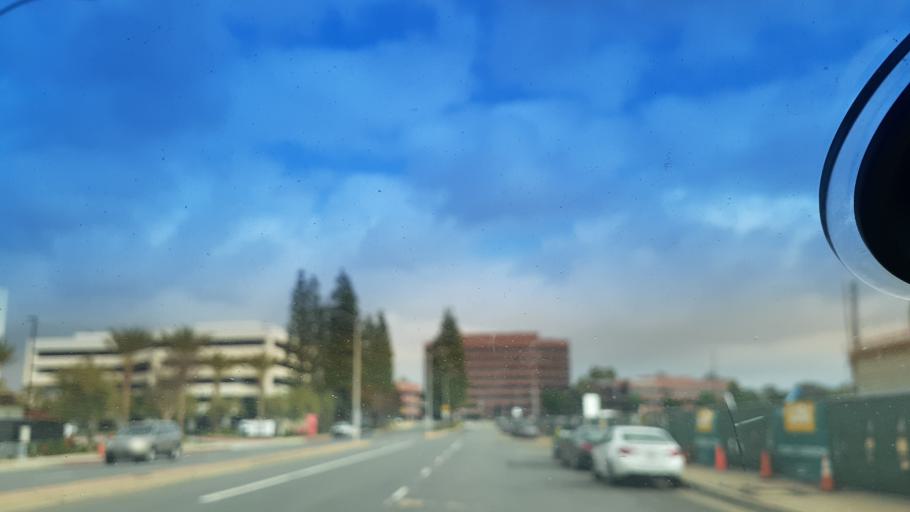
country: US
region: California
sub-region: Orange County
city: Orange
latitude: 33.7766
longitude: -117.8623
